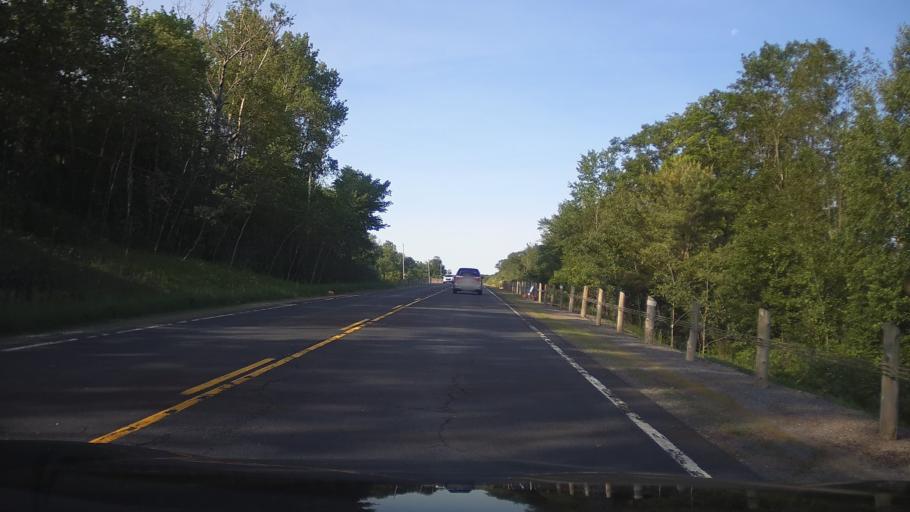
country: CA
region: Ontario
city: Greater Napanee
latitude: 44.6101
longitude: -77.1812
